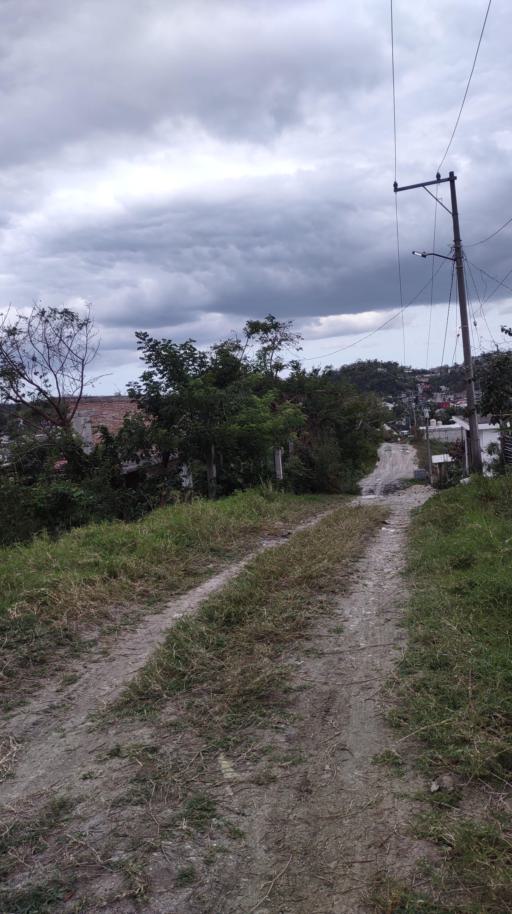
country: MX
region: Veracruz
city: Papantla de Olarte
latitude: 20.4313
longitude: -97.3388
